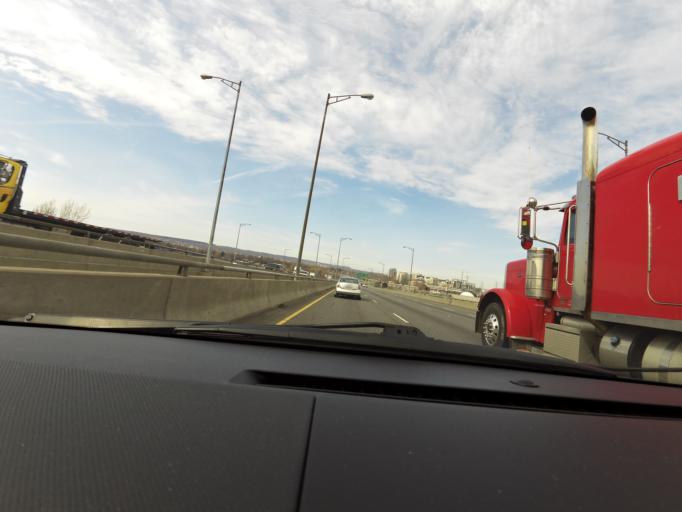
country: CA
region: Ontario
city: Hamilton
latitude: 43.3051
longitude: -79.8010
